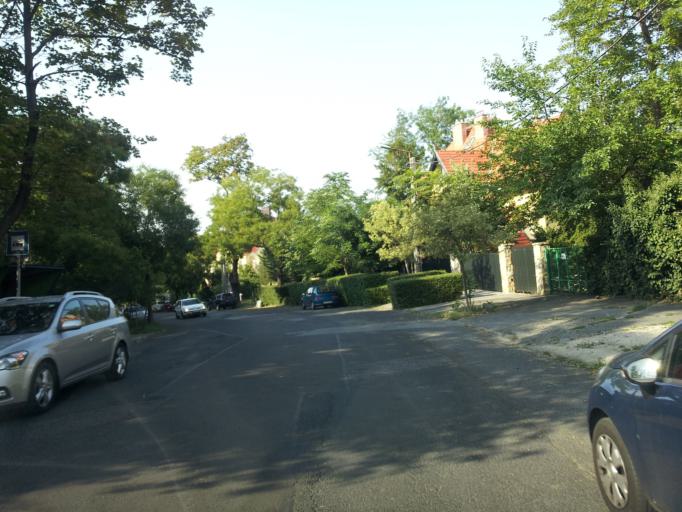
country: HU
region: Budapest
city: Budapest XII. keruelet
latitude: 47.5017
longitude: 19.0156
